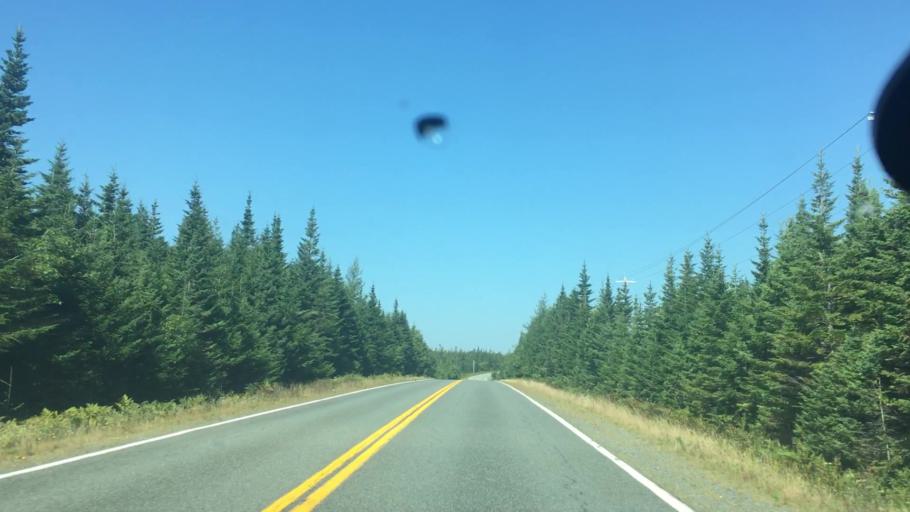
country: CA
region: Nova Scotia
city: Antigonish
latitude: 45.0046
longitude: -62.1030
